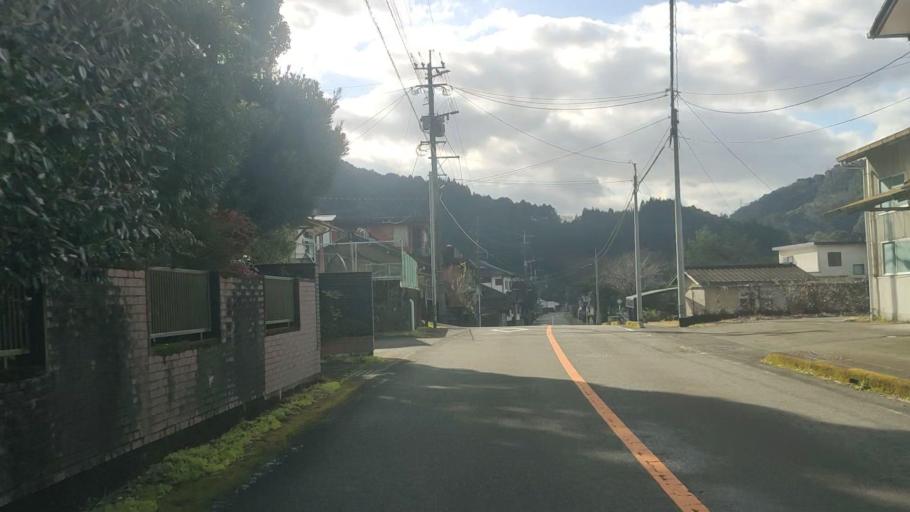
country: JP
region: Kumamoto
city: Hitoyoshi
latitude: 32.3075
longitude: 130.8479
